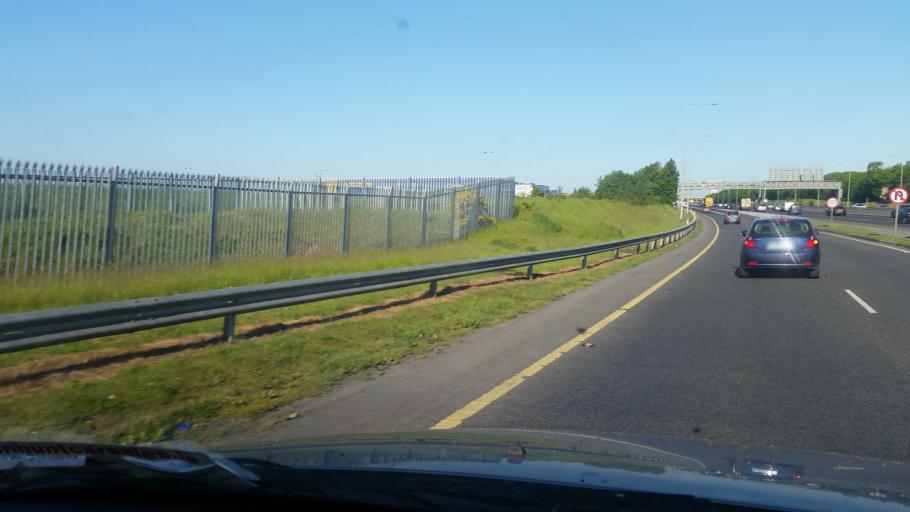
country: IE
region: Leinster
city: Ballymun
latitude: 53.4087
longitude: -6.2689
